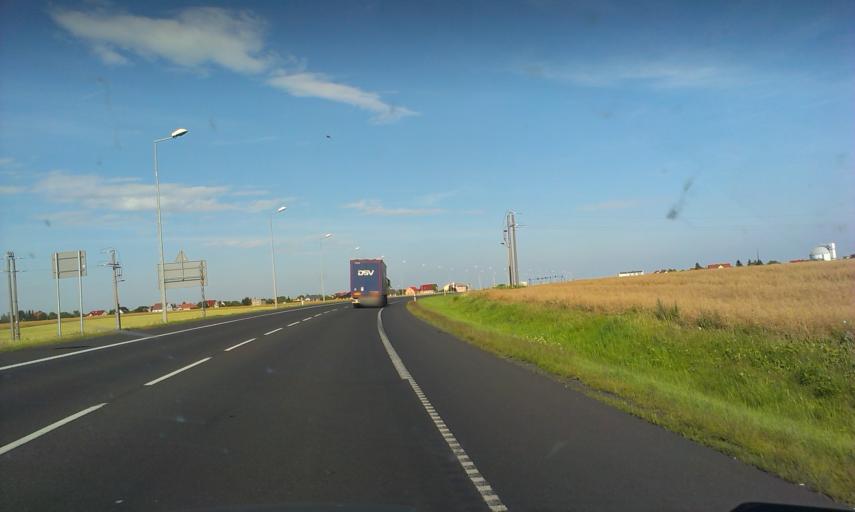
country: PL
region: Kujawsko-Pomorskie
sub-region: Powiat nakielski
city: Naklo nad Notecia
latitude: 53.1520
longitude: 17.5952
